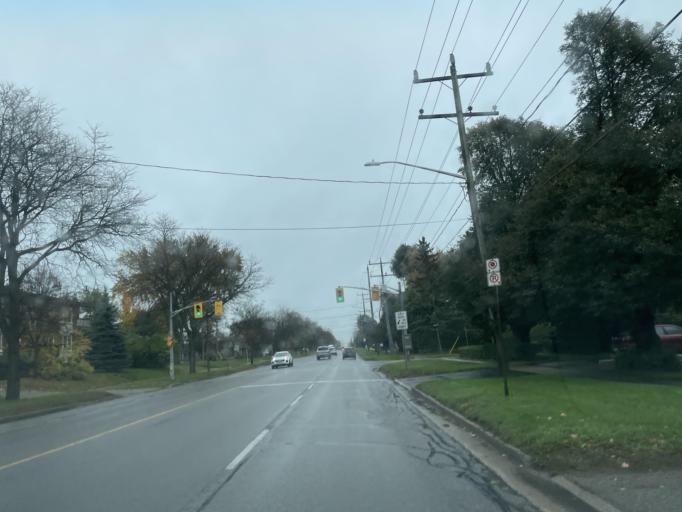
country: CA
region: Ontario
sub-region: Wellington County
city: Guelph
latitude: 43.5747
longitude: -80.2558
